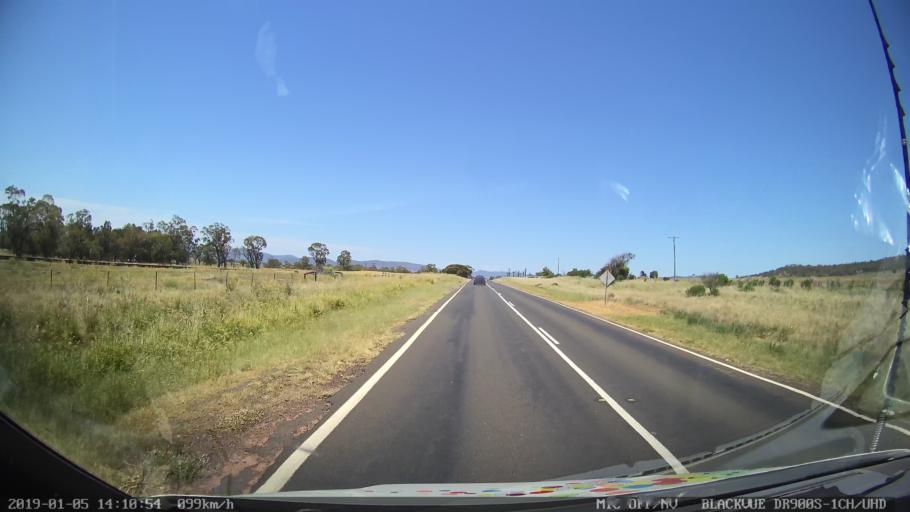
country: AU
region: New South Wales
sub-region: Gunnedah
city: Gunnedah
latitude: -31.2447
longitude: 150.4503
